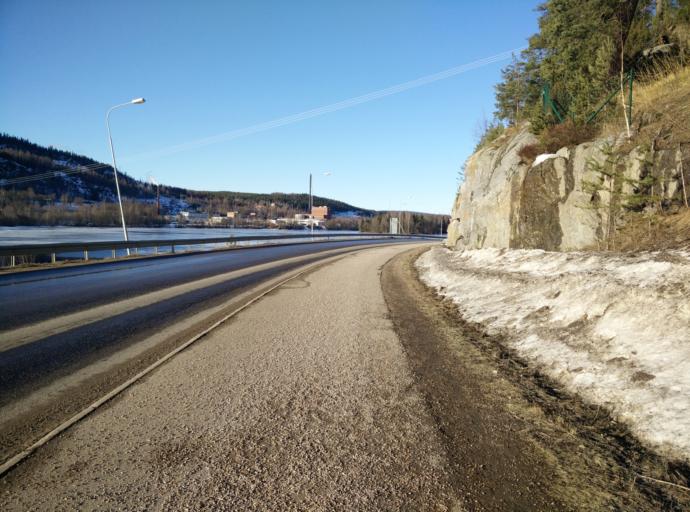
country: SE
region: Vaesternorrland
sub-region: Sundsvalls Kommun
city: Skottsund
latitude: 62.3021
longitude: 17.3849
